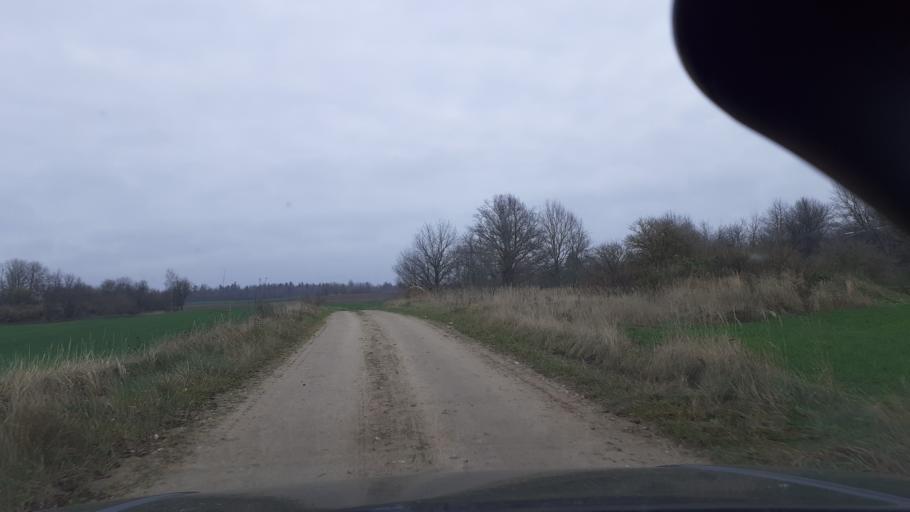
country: LV
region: Aizpute
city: Aizpute
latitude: 56.7864
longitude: 21.7601
